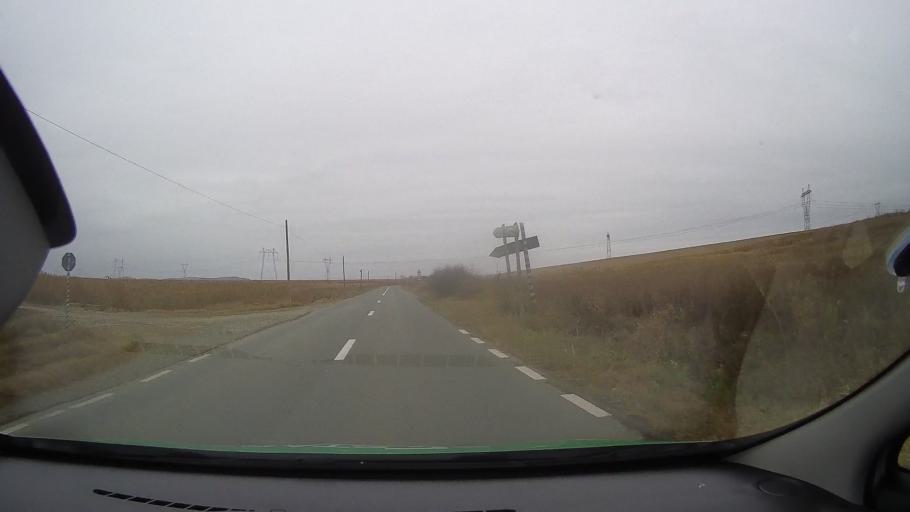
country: RO
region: Constanta
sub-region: Comuna Silistea
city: Silistea
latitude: 44.4330
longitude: 28.2191
